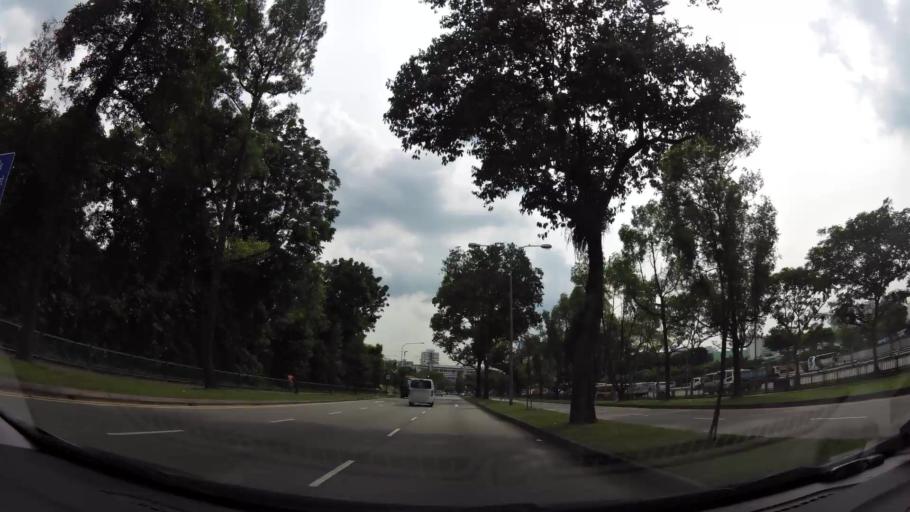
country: MY
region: Johor
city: Johor Bahru
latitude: 1.4478
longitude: 103.7775
